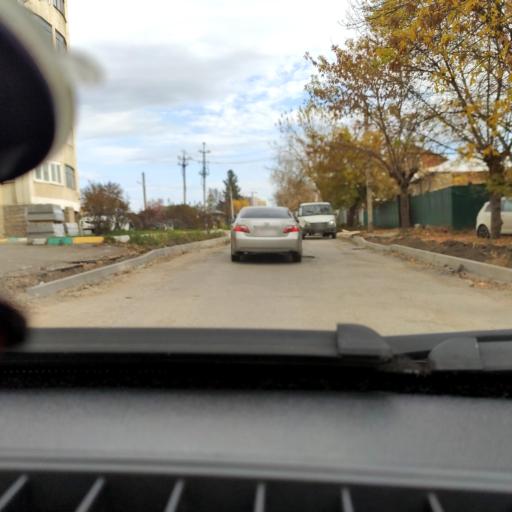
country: RU
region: Bashkortostan
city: Ufa
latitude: 54.7219
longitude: 55.9657
